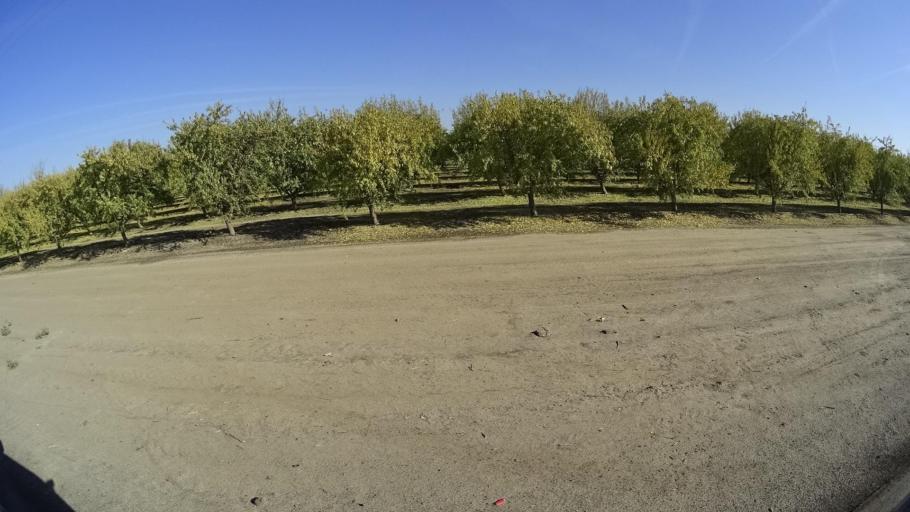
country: US
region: California
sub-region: Kern County
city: Wasco
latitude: 35.7000
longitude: -119.3839
